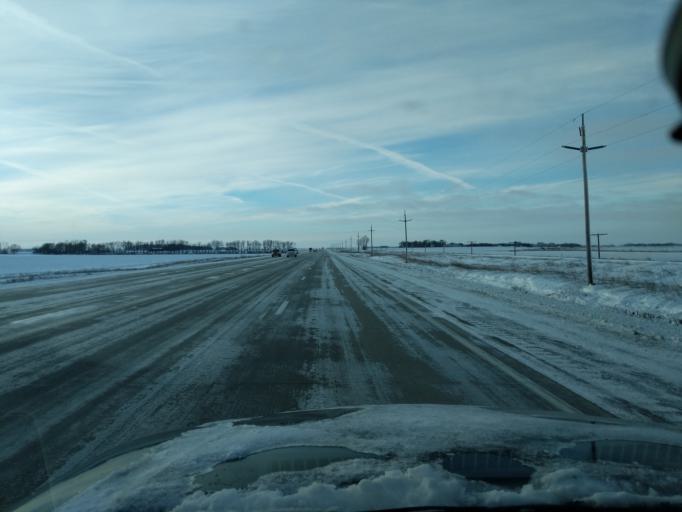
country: US
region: Minnesota
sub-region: Renville County
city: Hector
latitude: 44.7517
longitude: -94.7803
